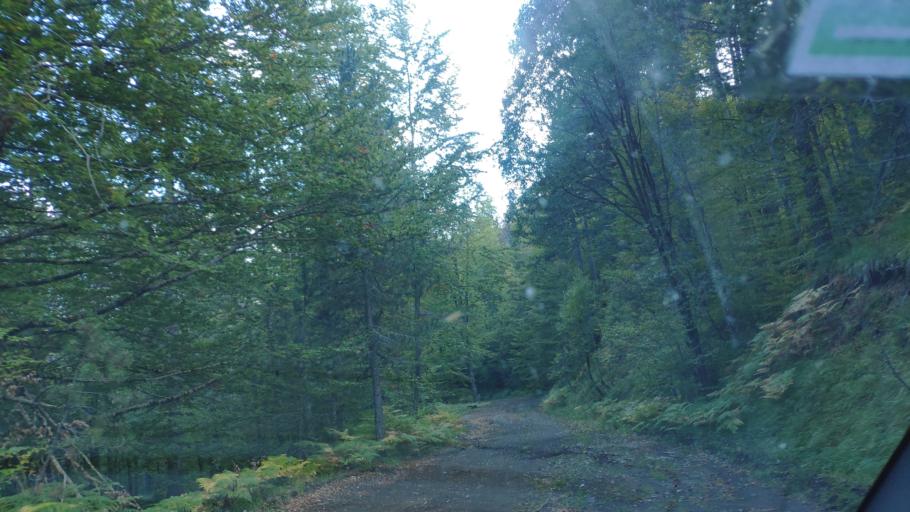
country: AL
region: Korce
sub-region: Rrethi i Devollit
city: Miras
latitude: 40.3464
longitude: 20.8994
